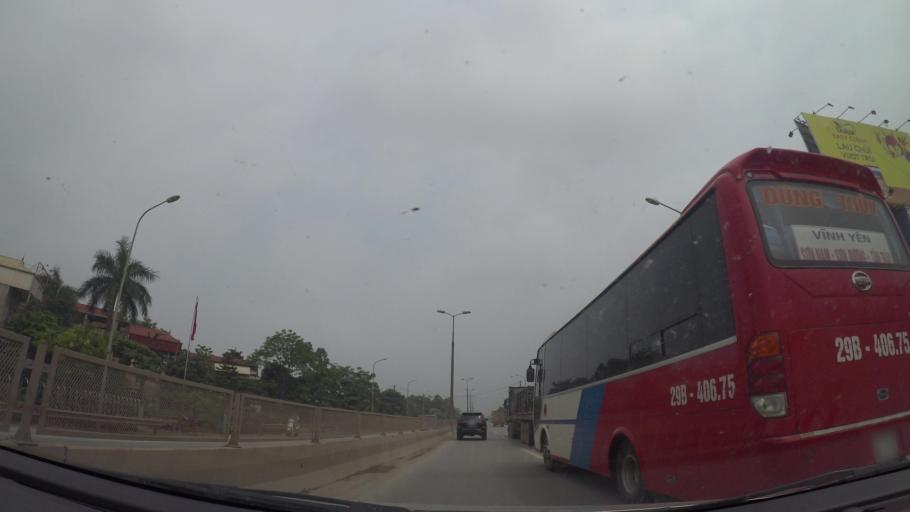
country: VN
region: Ha Noi
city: Tay Ho
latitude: 21.1179
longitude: 105.7839
